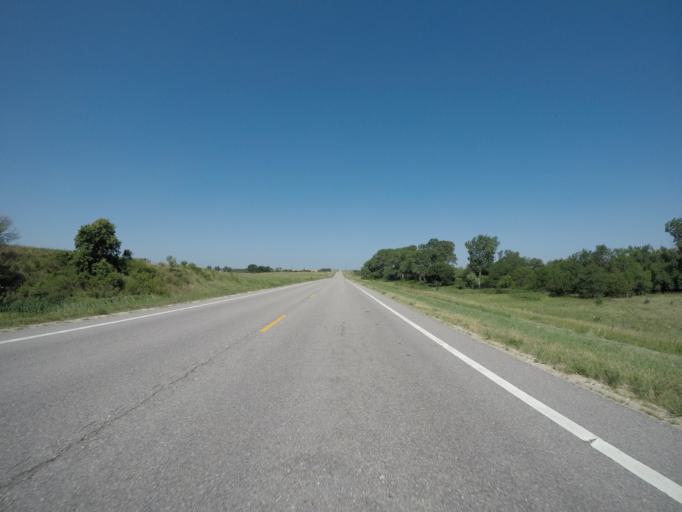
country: US
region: Kansas
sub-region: Cloud County
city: Concordia
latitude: 39.3647
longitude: -97.5448
